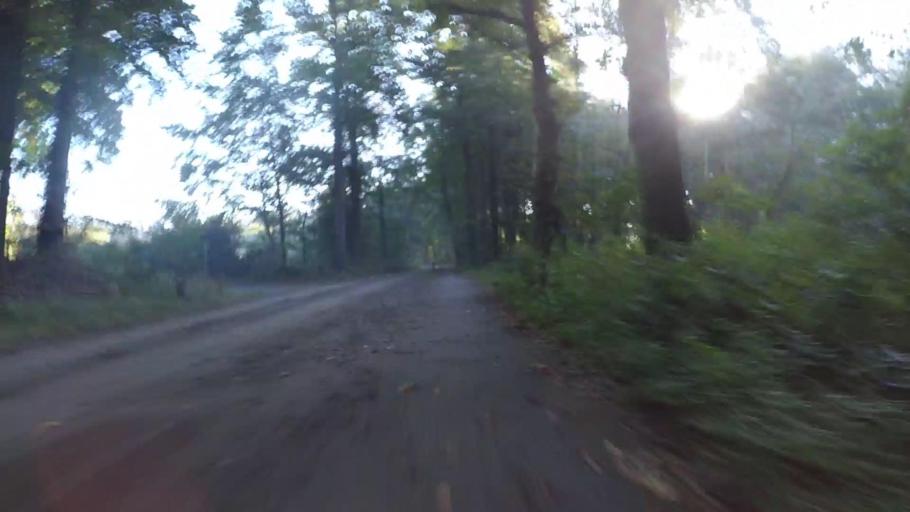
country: NL
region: Gelderland
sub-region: Gemeente Epe
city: Vaassen
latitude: 52.2880
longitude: 5.9154
